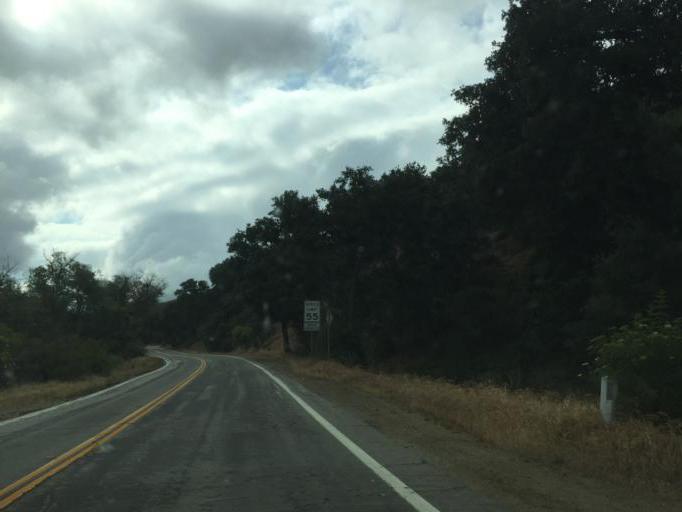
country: US
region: California
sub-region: Los Angeles County
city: Green Valley
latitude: 34.5841
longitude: -118.3586
